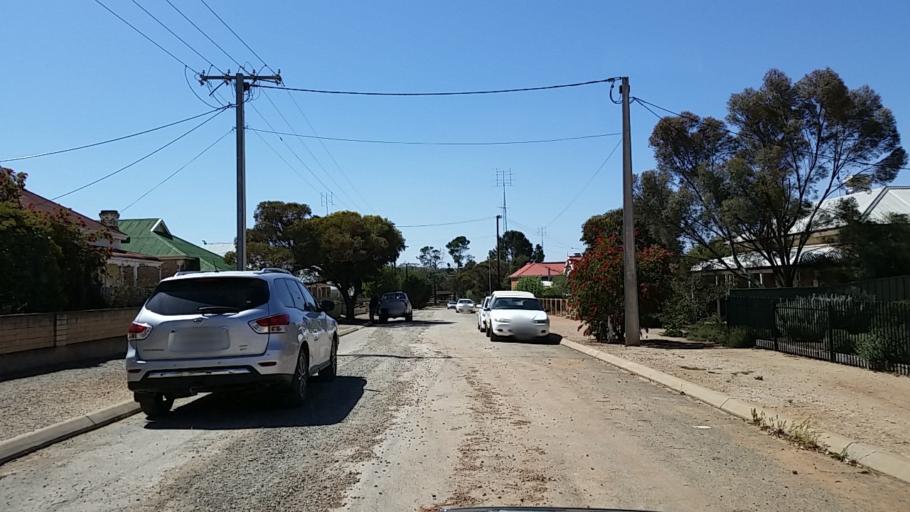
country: AU
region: South Australia
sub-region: Peterborough
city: Peterborough
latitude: -32.9768
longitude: 138.8361
